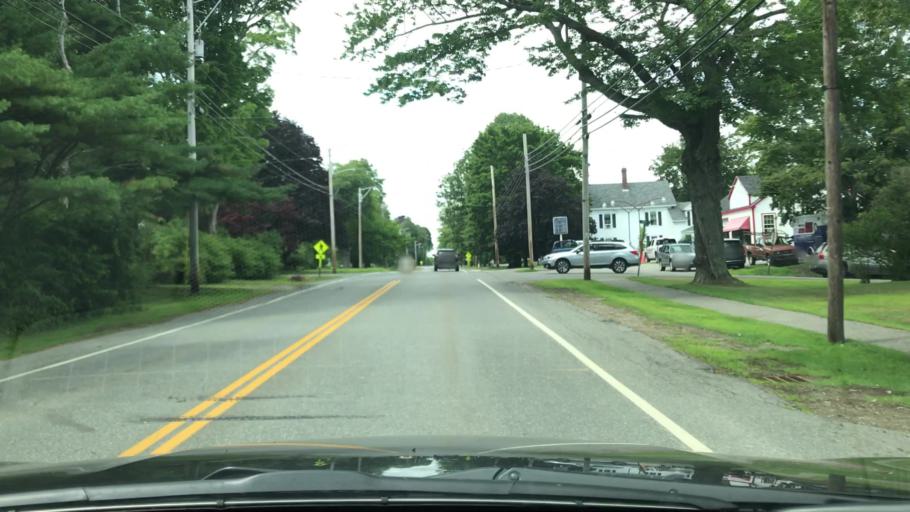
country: US
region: Maine
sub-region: Waldo County
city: Belfast
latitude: 44.4176
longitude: -68.9979
